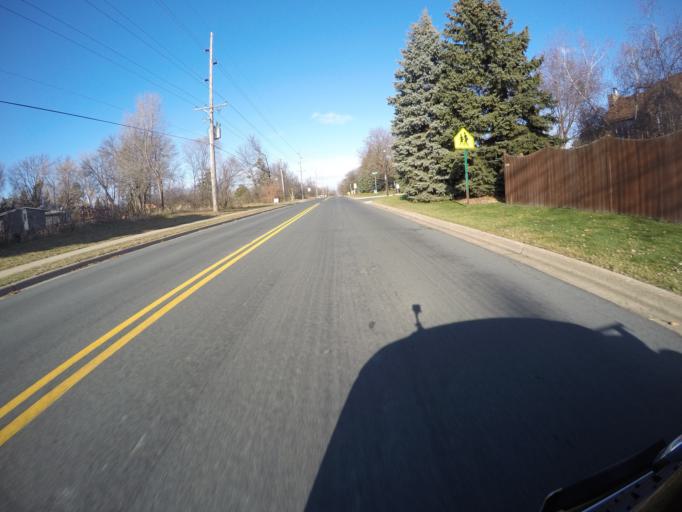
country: US
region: Minnesota
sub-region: Hennepin County
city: Eden Prairie
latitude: 44.8745
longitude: -93.4957
